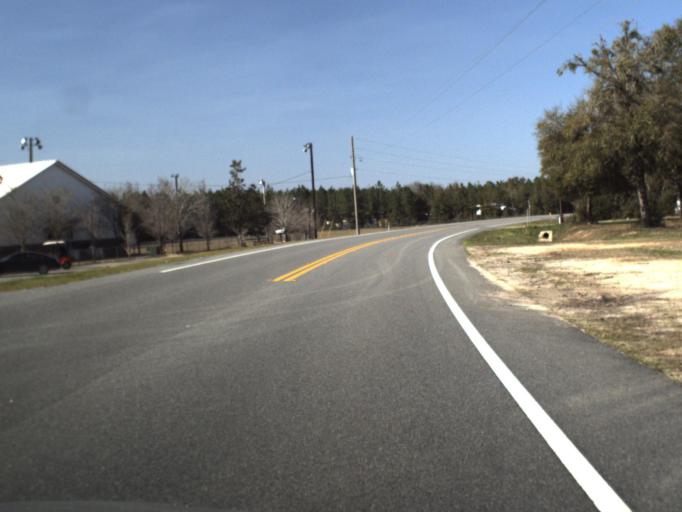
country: US
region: Florida
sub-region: Gulf County
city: Wewahitchka
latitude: 30.2651
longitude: -85.2417
